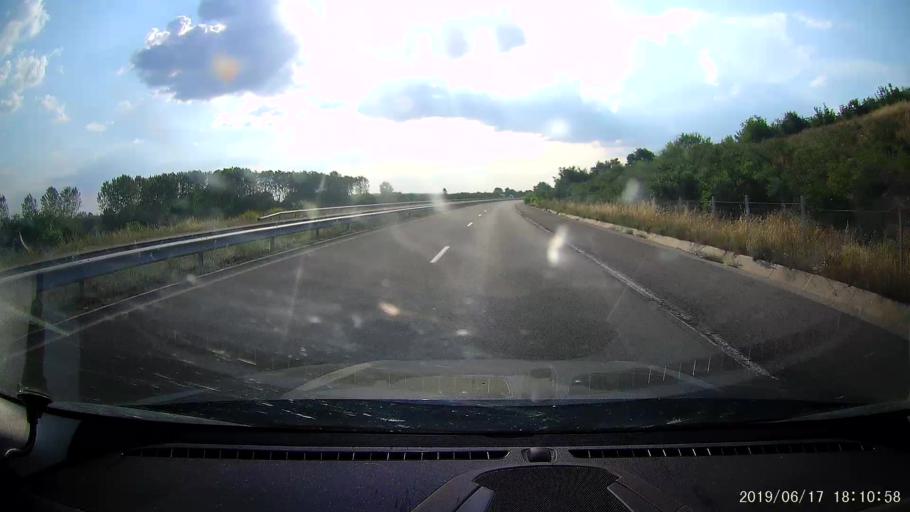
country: BG
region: Khaskovo
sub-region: Obshtina Lyubimets
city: Lyubimets
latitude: 41.8780
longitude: 26.0628
